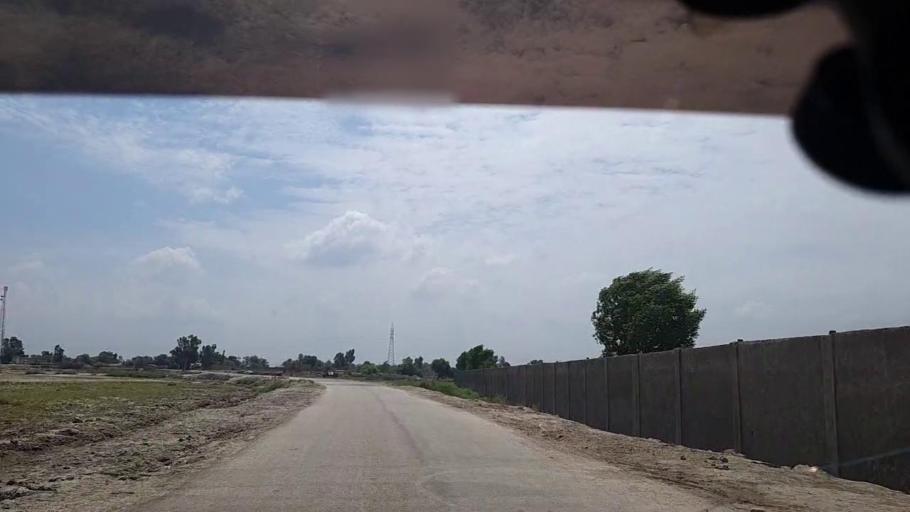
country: PK
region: Sindh
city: Ghauspur
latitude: 28.0912
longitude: 68.9605
